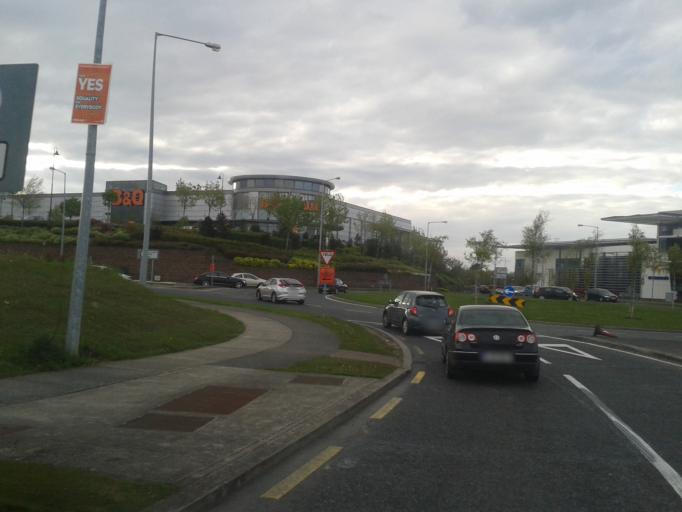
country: IE
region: Leinster
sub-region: Fingal County
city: Swords
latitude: 53.4470
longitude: -6.2201
